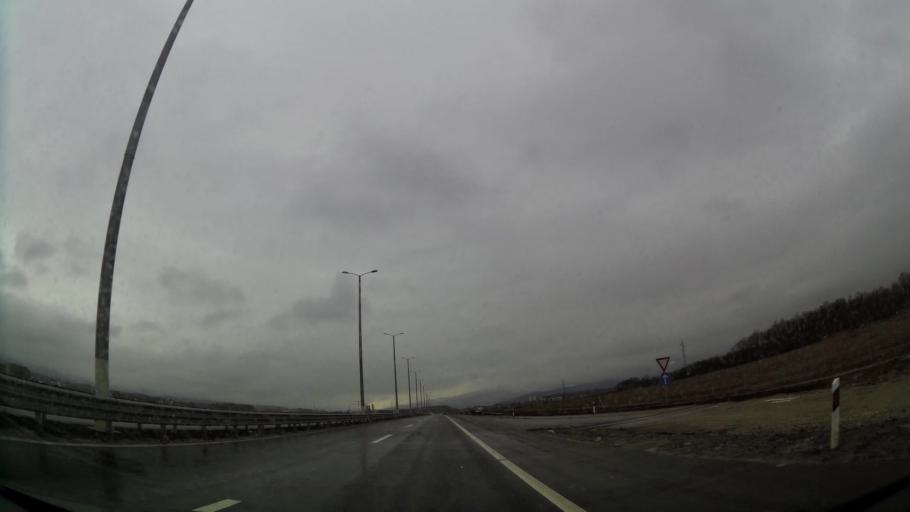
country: XK
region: Ferizaj
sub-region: Komuna e Kacanikut
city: Kacanik
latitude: 42.2885
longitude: 21.2072
